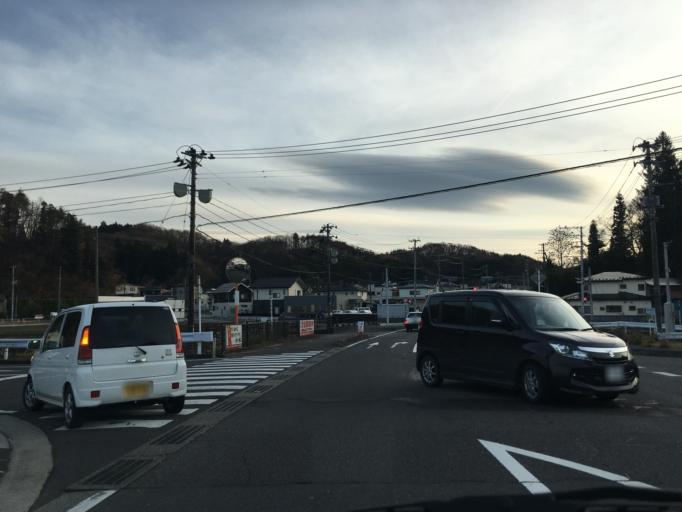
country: JP
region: Fukushima
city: Ishikawa
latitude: 37.1178
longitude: 140.2284
